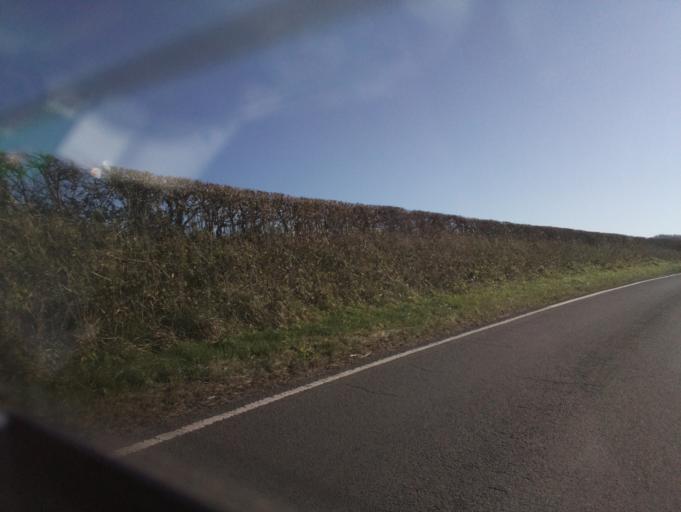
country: GB
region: England
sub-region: Dorset
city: Dorchester
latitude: 50.8188
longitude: -2.4561
